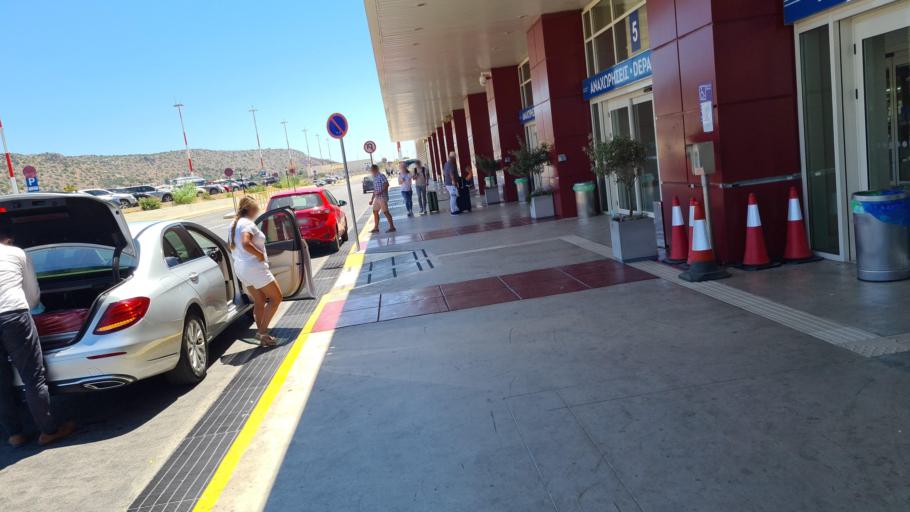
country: GR
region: Crete
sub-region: Nomos Chanias
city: Mouzouras
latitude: 35.5401
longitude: 24.1410
